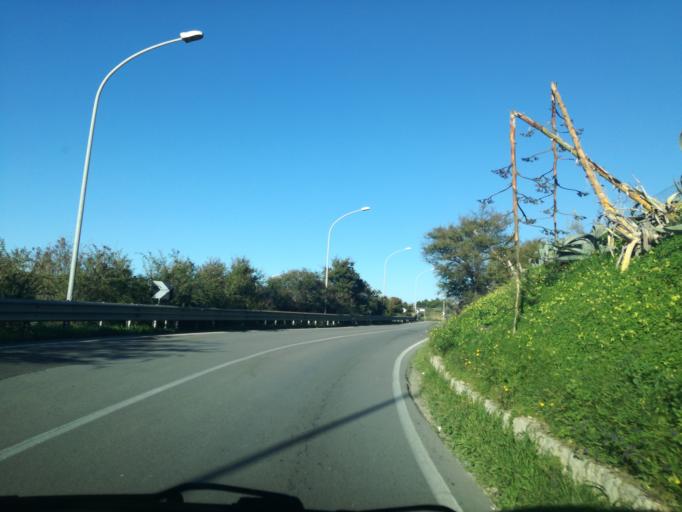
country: IT
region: Sicily
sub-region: Provincia di Caltanissetta
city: Gela
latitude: 37.1034
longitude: 14.1577
